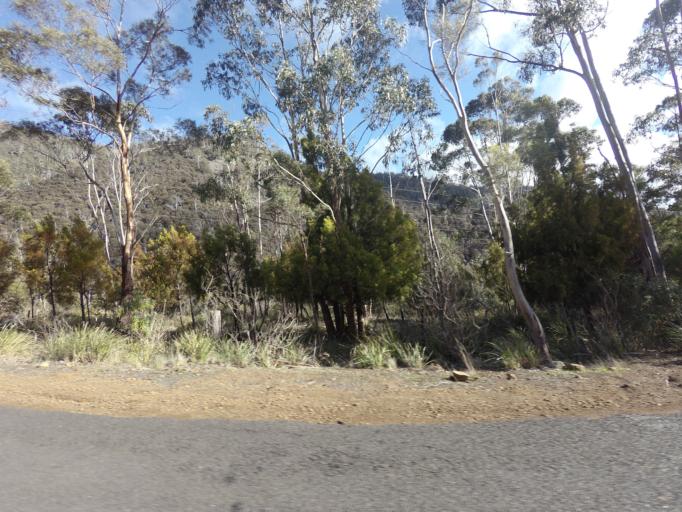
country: AU
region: Tasmania
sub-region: Glenorchy
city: Berriedale
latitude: -42.8159
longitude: 147.1759
